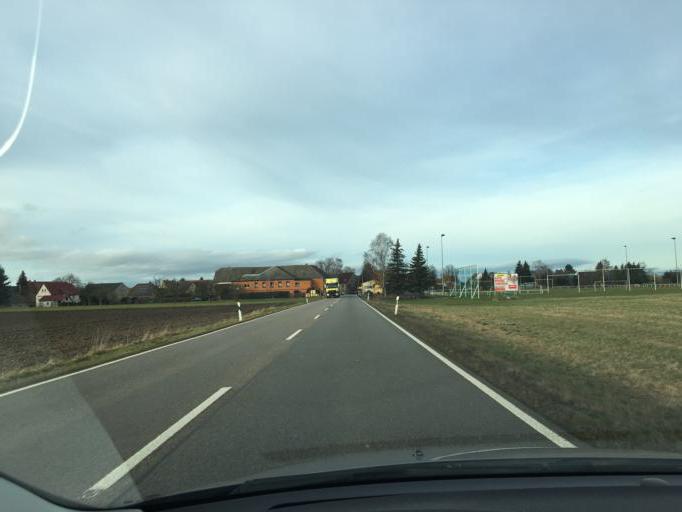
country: DE
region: Thuringia
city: Fockendorf
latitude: 51.0590
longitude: 12.4545
